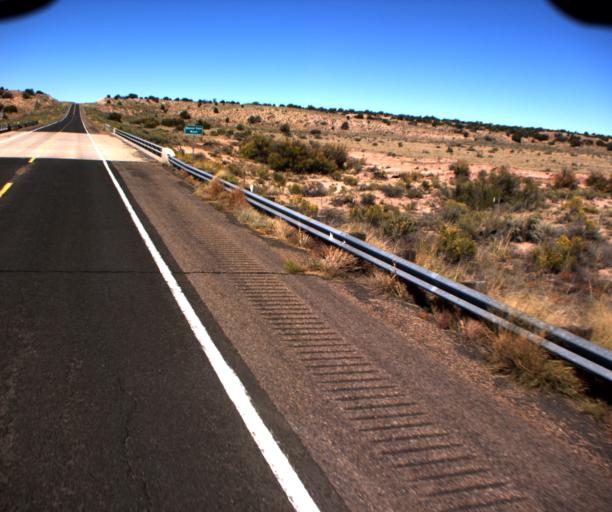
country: US
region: Arizona
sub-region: Navajo County
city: Snowflake
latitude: 34.6688
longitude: -109.7230
